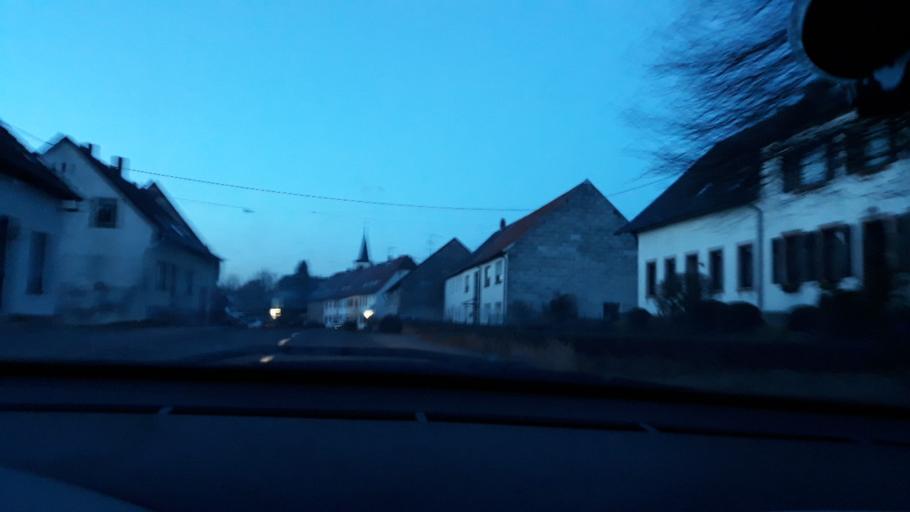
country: DE
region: Saarland
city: Gersheim
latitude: 49.1822
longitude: 7.1633
